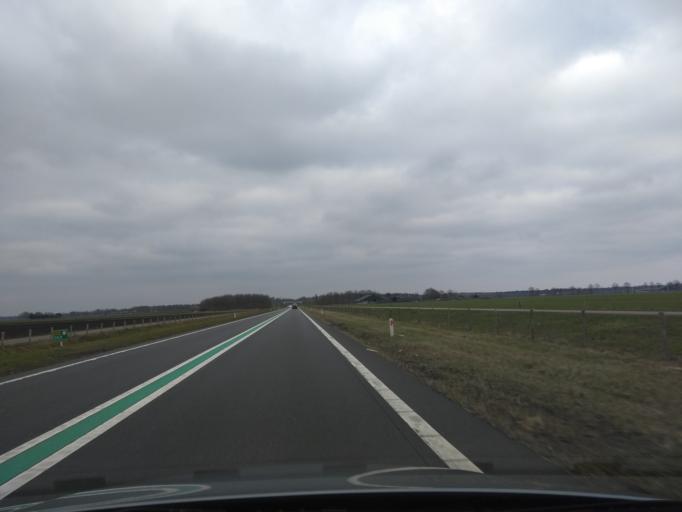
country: NL
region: Overijssel
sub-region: Gemeente Twenterand
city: Magele
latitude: 52.5592
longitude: 6.4982
